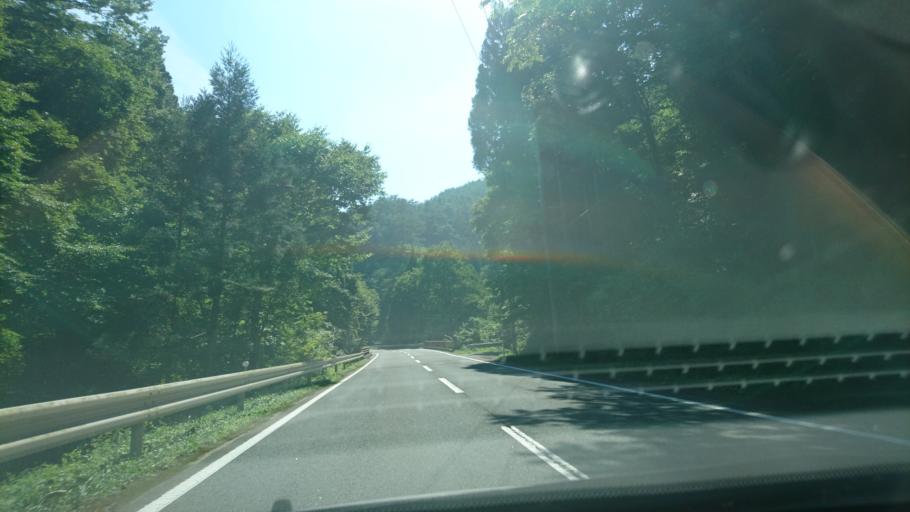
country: JP
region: Iwate
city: Ofunato
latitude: 39.0213
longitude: 141.4990
